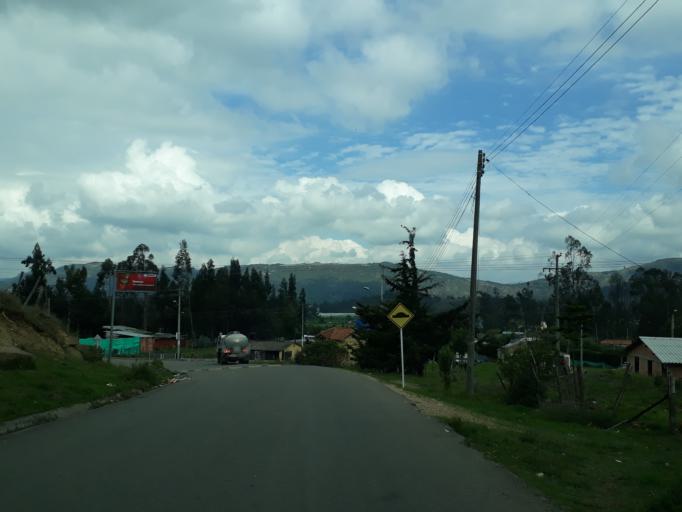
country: CO
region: Cundinamarca
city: Suesca
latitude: 5.0847
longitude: -73.7912
